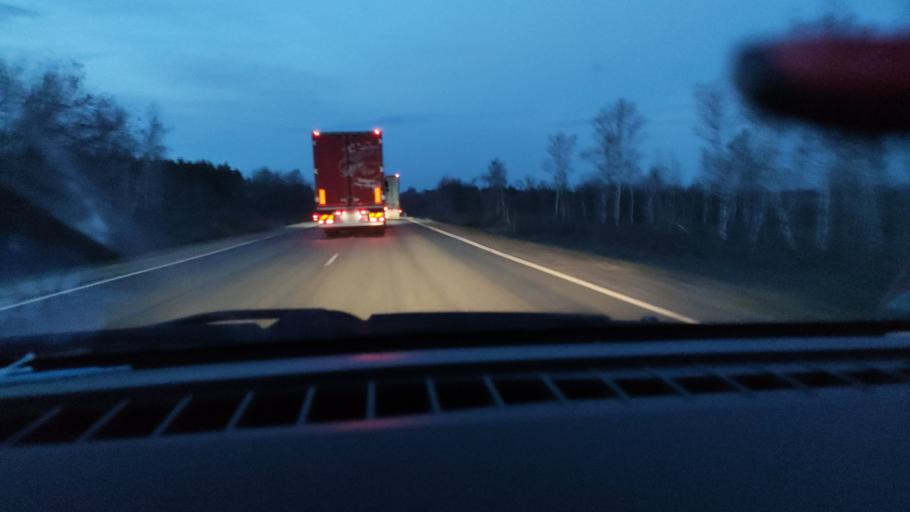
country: RU
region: Saratov
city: Sennoy
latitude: 52.1142
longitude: 46.8350
